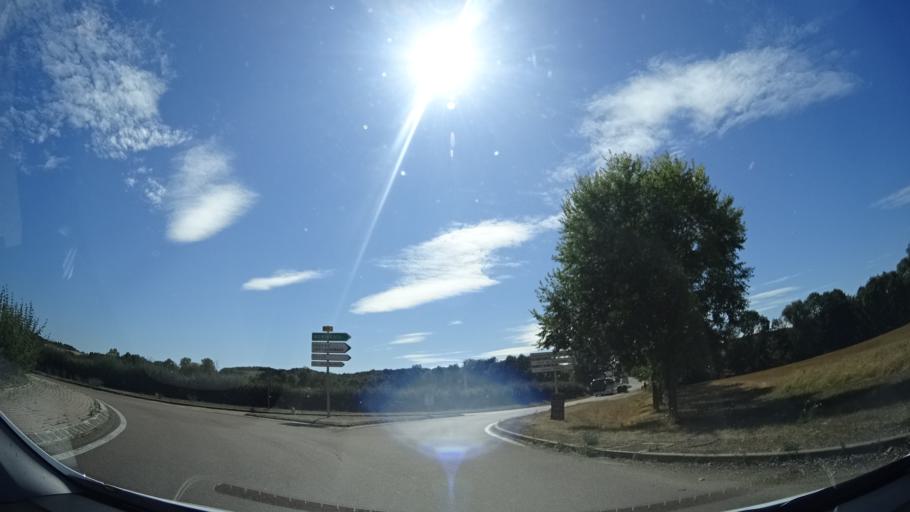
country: FR
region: Bourgogne
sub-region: Departement de l'Yonne
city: Saint-Julien-du-Sault
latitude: 47.9385
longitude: 3.2426
